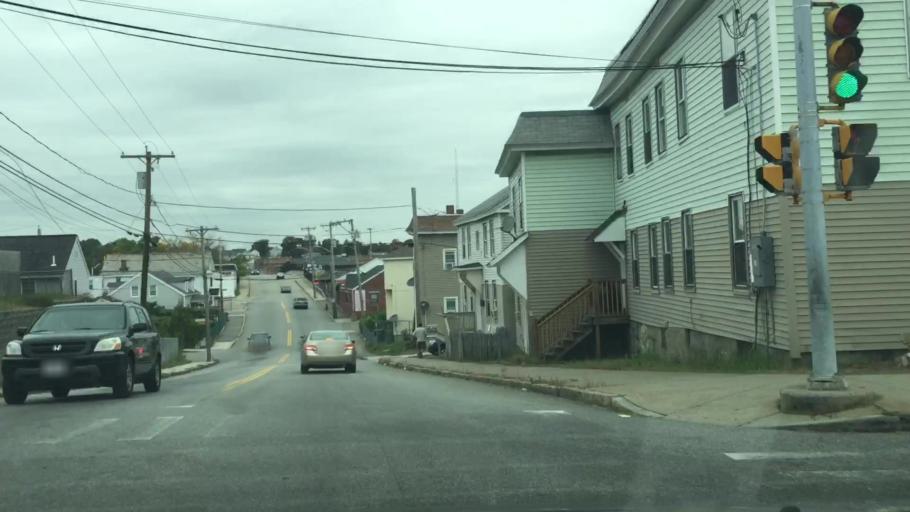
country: US
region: Massachusetts
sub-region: Middlesex County
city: Lowell
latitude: 42.6385
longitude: -71.3247
